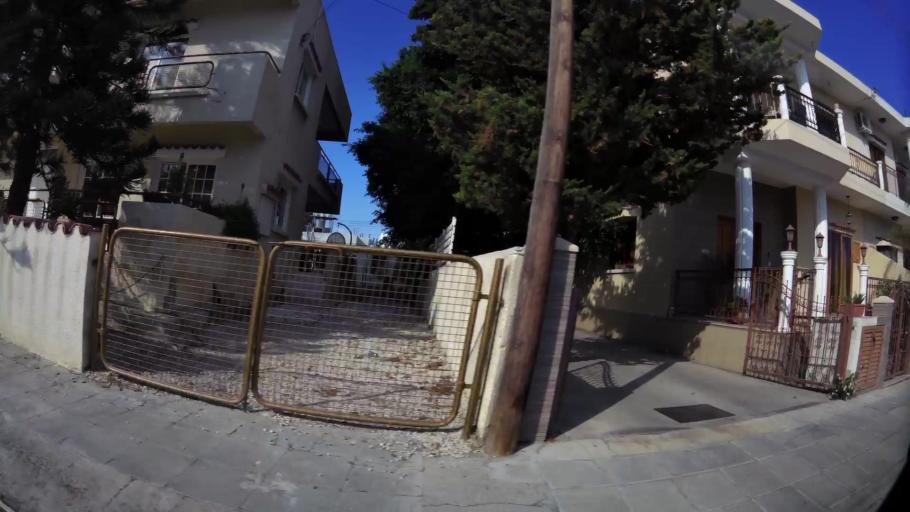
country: CY
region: Larnaka
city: Livadia
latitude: 34.9486
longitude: 33.6237
